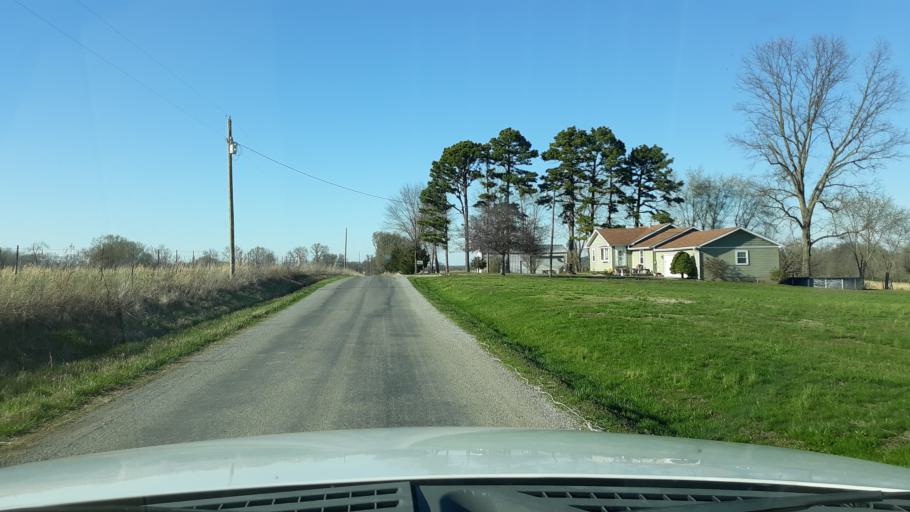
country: US
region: Illinois
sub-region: Saline County
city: Harrisburg
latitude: 37.7817
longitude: -88.6012
